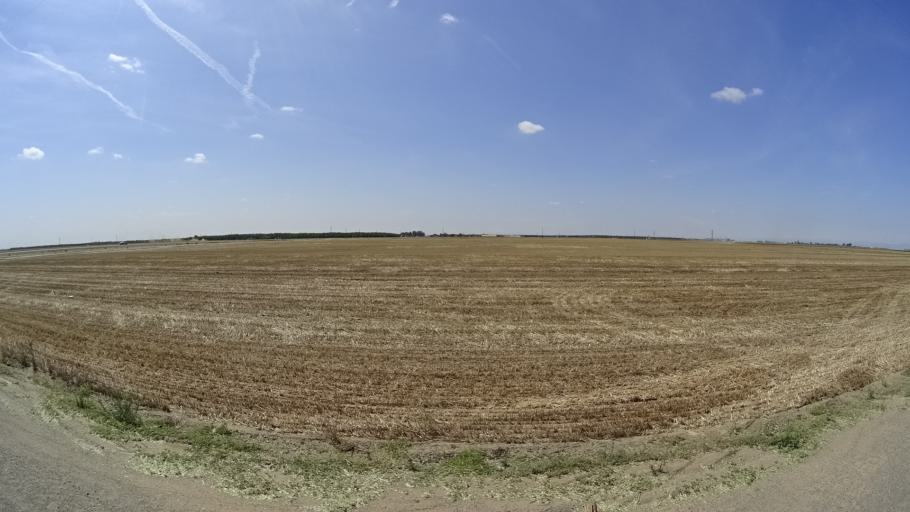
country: US
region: California
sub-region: Kings County
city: Home Garden
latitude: 36.2694
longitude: -119.6027
